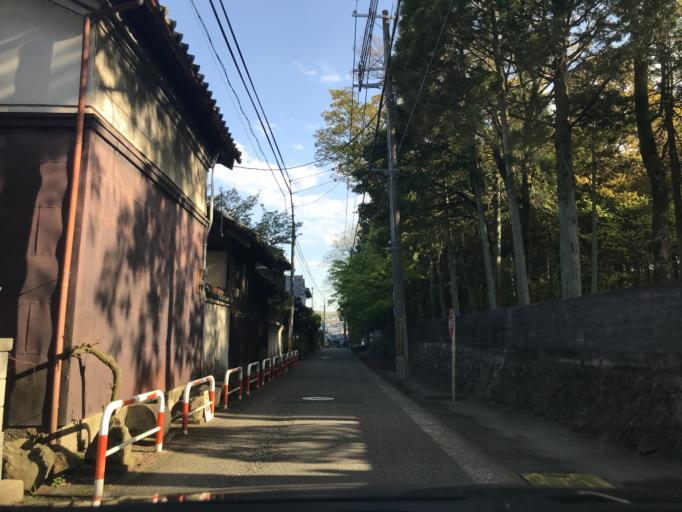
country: JP
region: Hyogo
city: Kawanishi
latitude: 34.8618
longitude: 135.4036
